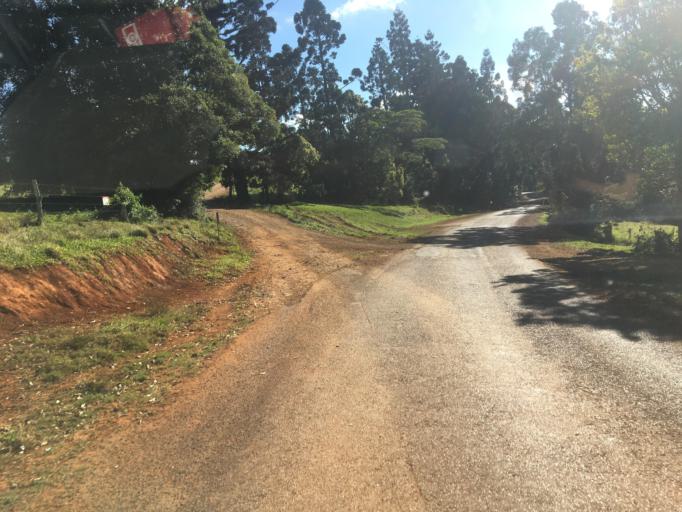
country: AU
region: Queensland
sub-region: Tablelands
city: Ravenshoe
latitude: -17.6036
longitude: 145.5629
